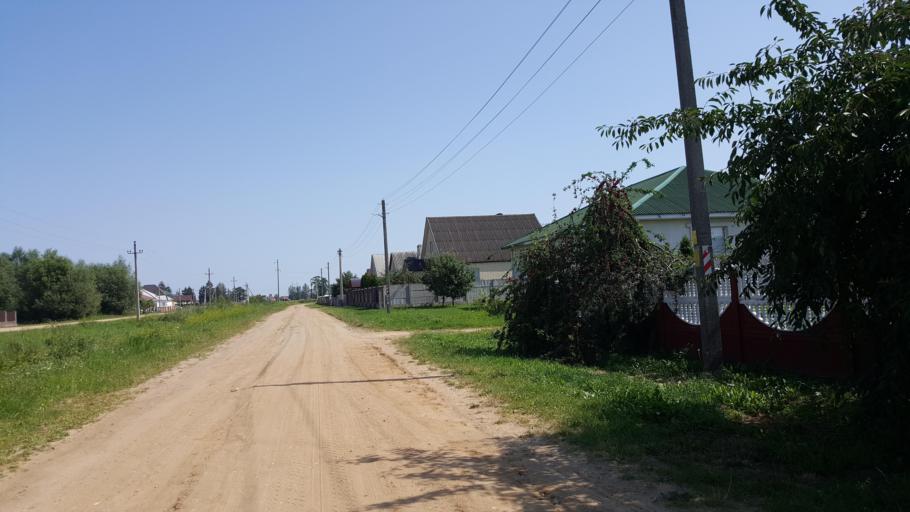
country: BY
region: Brest
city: Zhabinka
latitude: 52.2057
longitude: 23.9993
